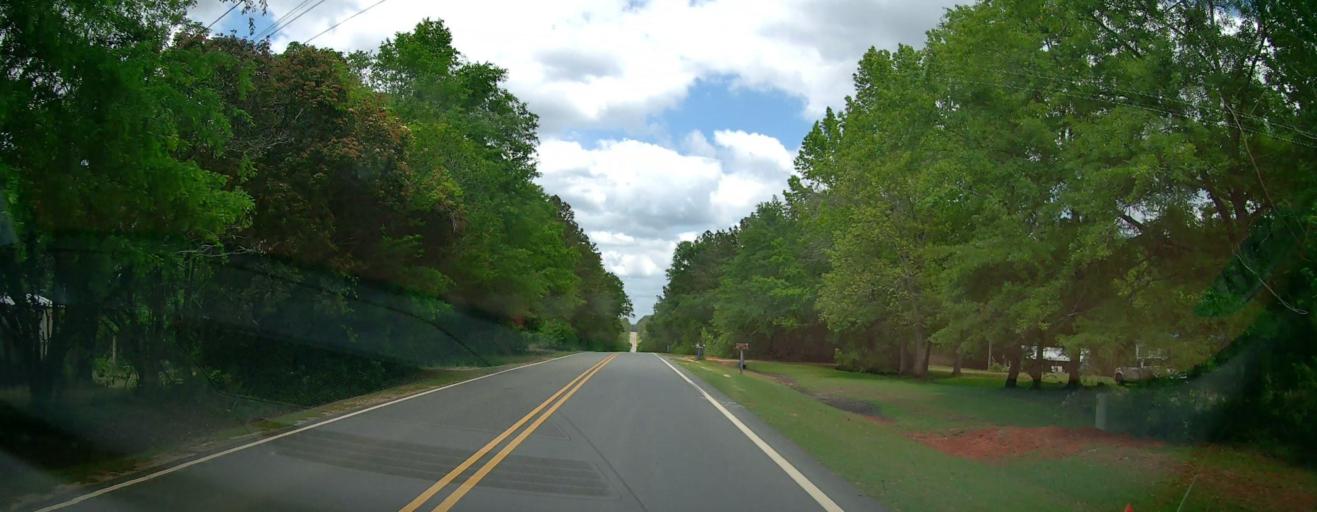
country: US
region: Georgia
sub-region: Laurens County
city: Dublin
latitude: 32.6204
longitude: -82.9735
